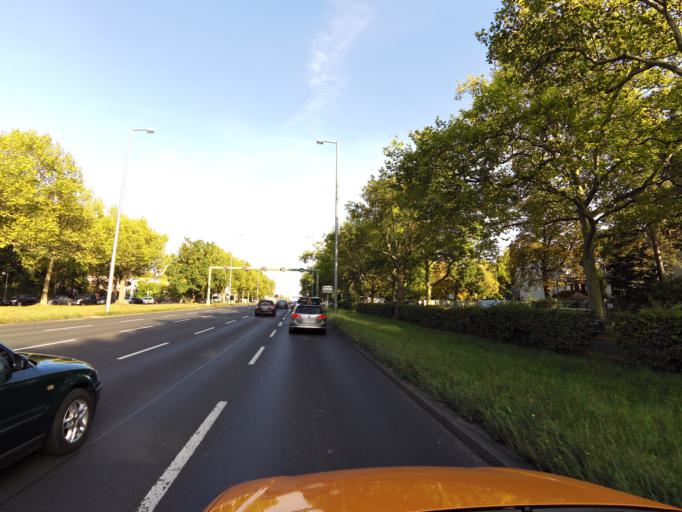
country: DE
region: Berlin
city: Westend
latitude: 52.5081
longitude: 13.2528
